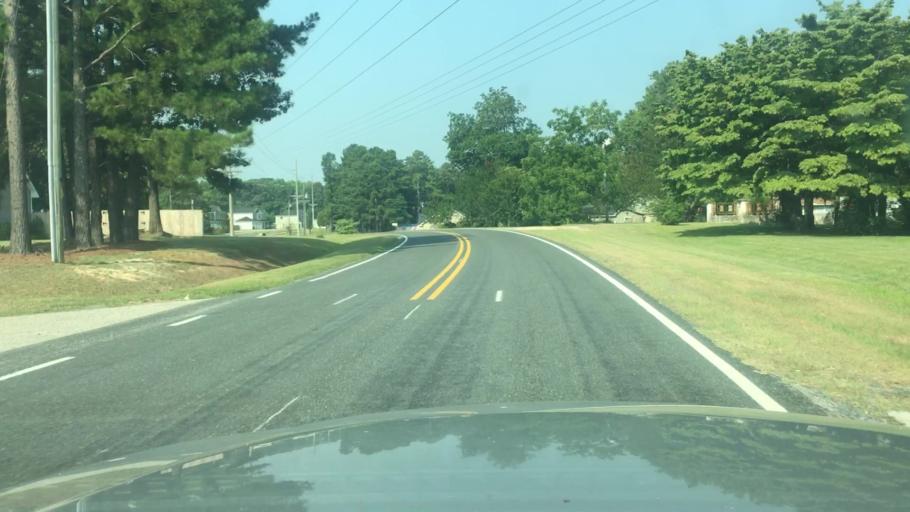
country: US
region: North Carolina
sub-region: Cumberland County
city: Hope Mills
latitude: 34.9026
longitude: -78.8743
